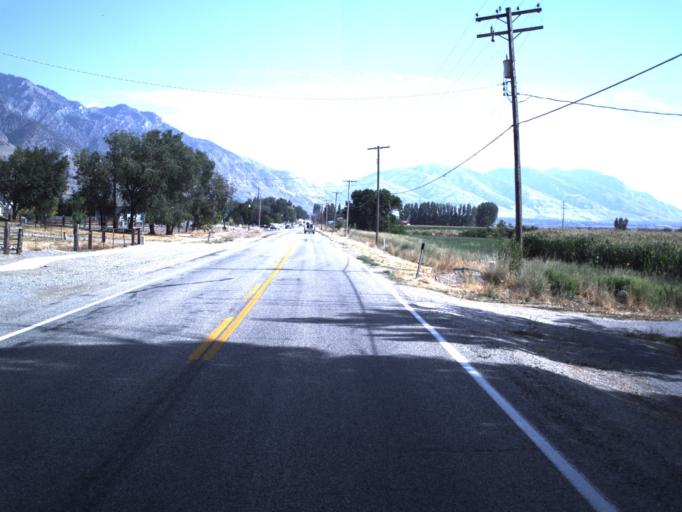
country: US
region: Utah
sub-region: Box Elder County
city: Honeyville
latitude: 41.6185
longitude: -112.0689
